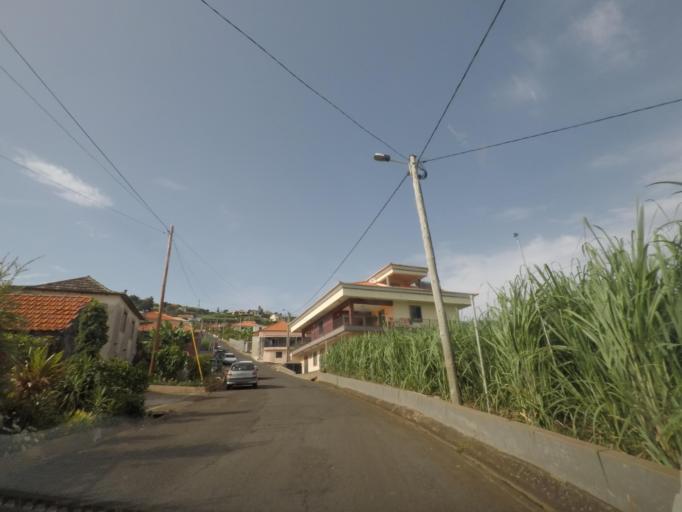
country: PT
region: Madeira
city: Ponta do Sol
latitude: 32.6936
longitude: -17.1164
